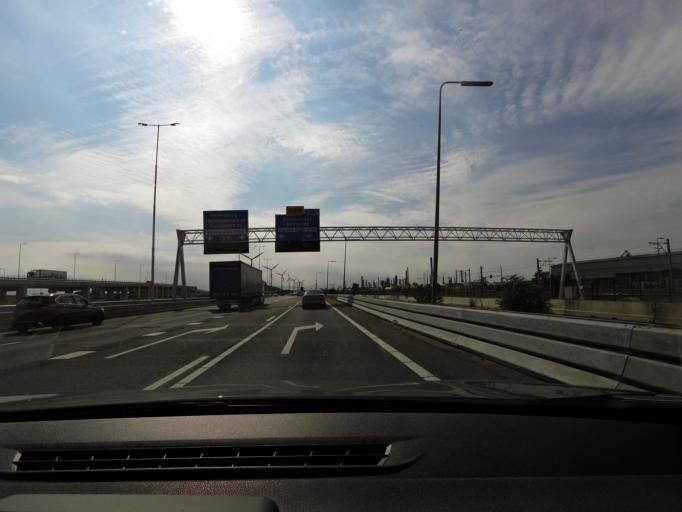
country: NL
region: South Holland
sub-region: Gemeente Spijkenisse
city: Spijkenisse
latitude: 51.8698
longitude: 4.3176
